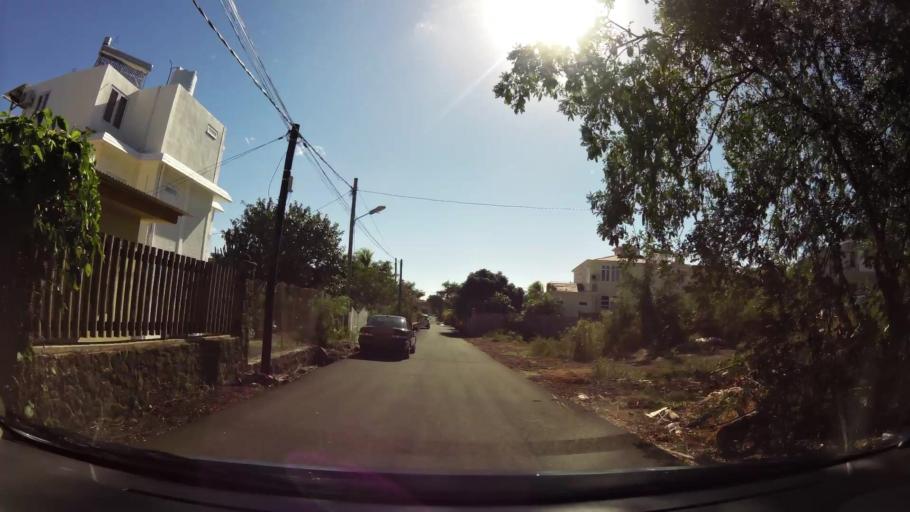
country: MU
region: Black River
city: Flic en Flac
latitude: -20.2668
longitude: 57.3758
